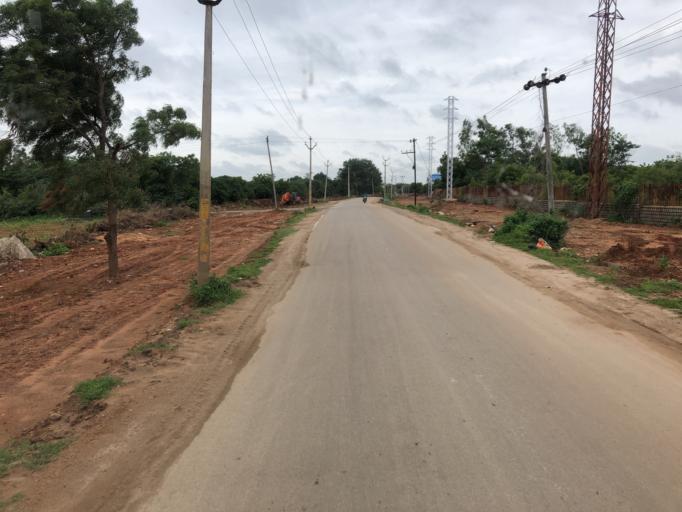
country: IN
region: Telangana
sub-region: Medak
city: Serilingampalle
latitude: 17.4319
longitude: 78.2984
